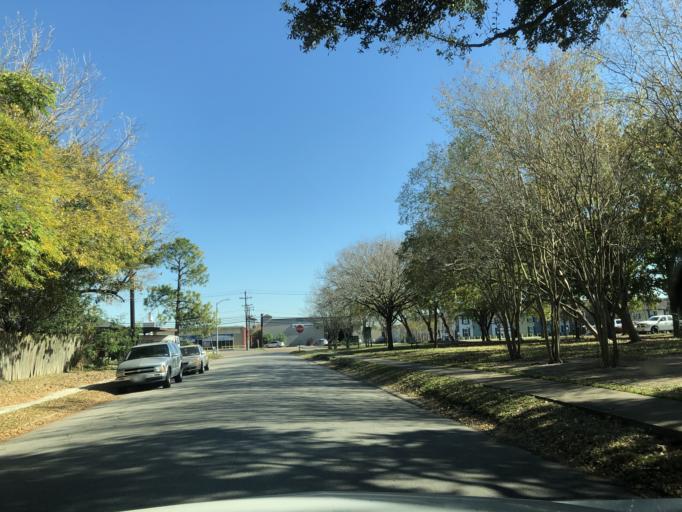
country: US
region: Texas
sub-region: Harris County
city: Bellaire
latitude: 29.6973
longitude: -95.4940
